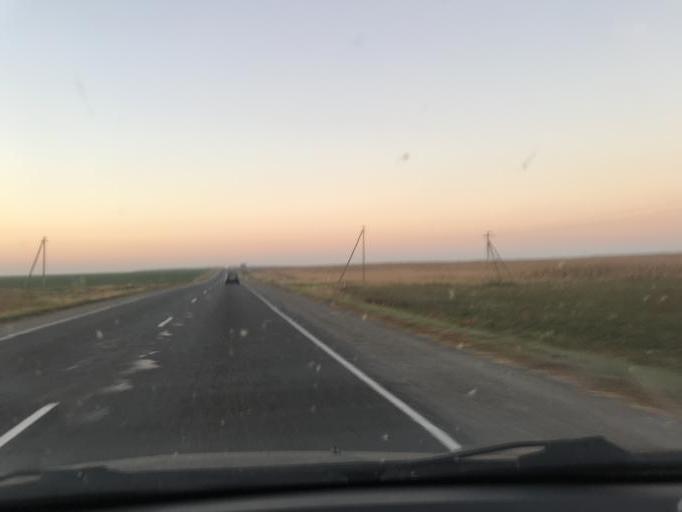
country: BY
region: Gomel
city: Horad Rechytsa
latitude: 52.2806
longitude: 30.4725
